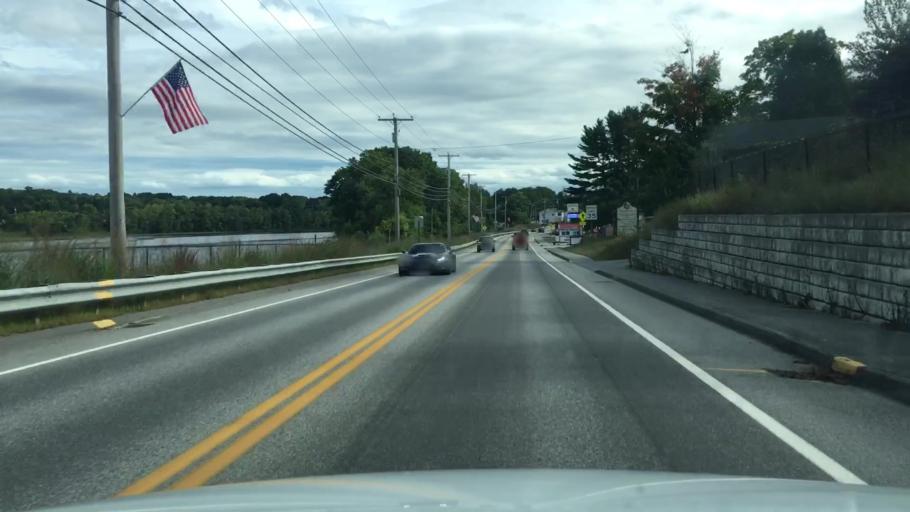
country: US
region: Maine
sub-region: Kennebec County
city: Farmingdale
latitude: 44.2492
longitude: -69.7717
